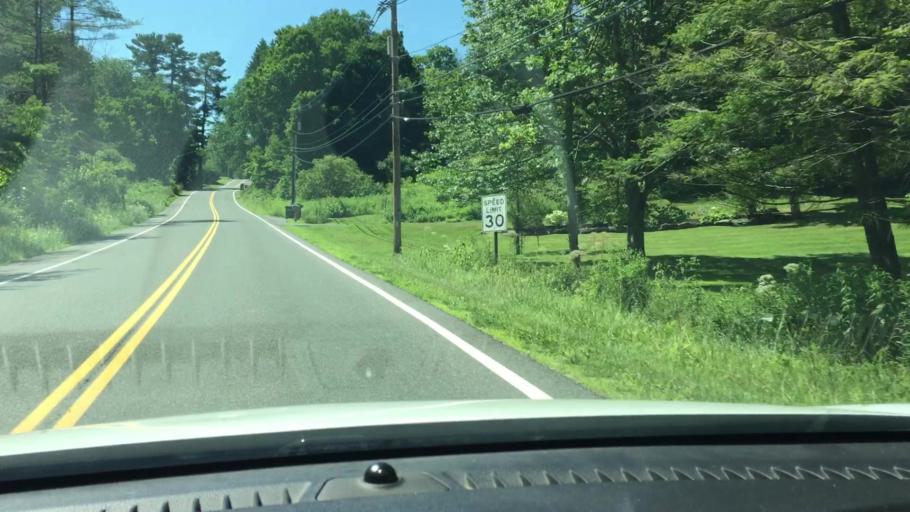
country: US
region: Massachusetts
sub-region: Berkshire County
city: Lenox
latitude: 42.3639
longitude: -73.2597
